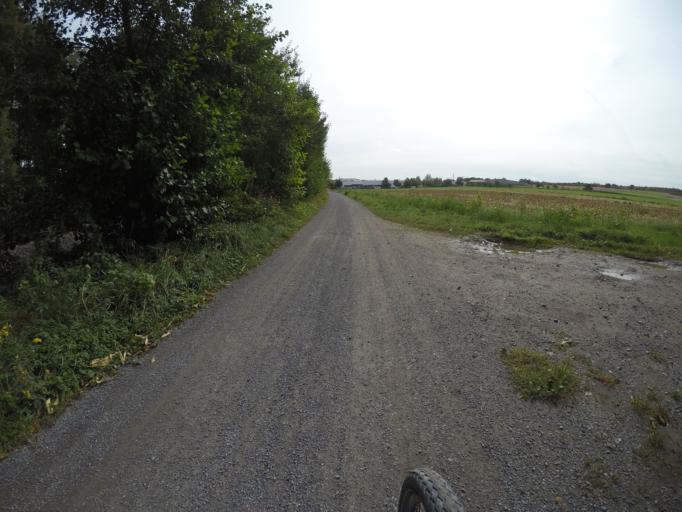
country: DE
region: Baden-Wuerttemberg
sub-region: Karlsruhe Region
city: Zaisenhausen
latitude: 49.1176
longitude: 8.7340
